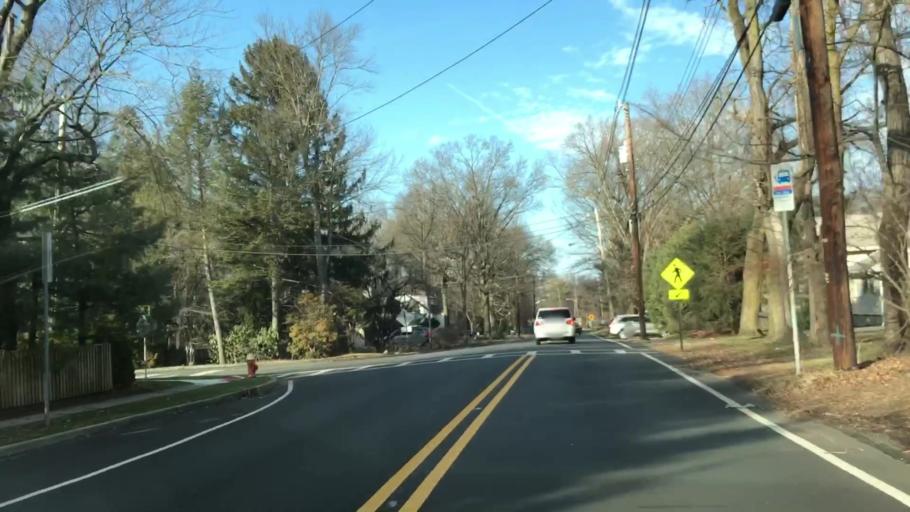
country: US
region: New Jersey
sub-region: Bergen County
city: Harrington Park
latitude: 40.9802
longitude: -73.9726
